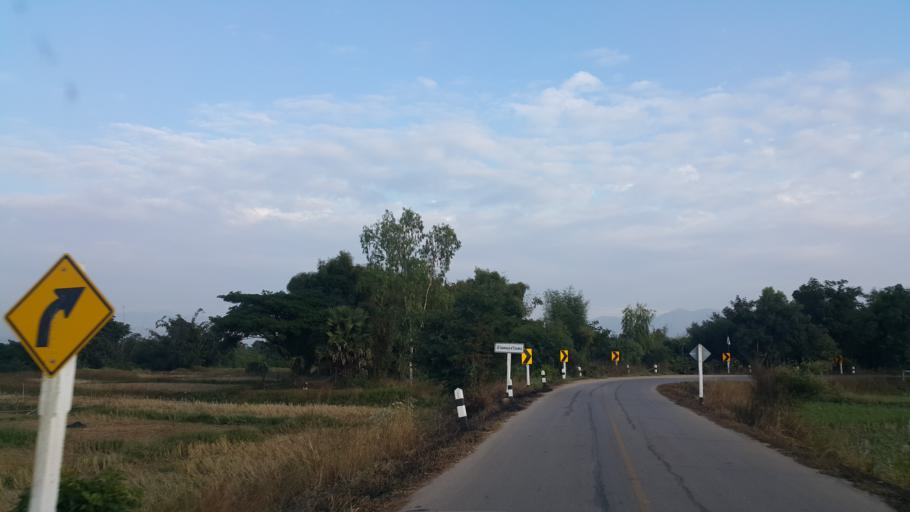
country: TH
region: Lampang
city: Sop Prap
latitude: 17.9084
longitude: 99.3291
